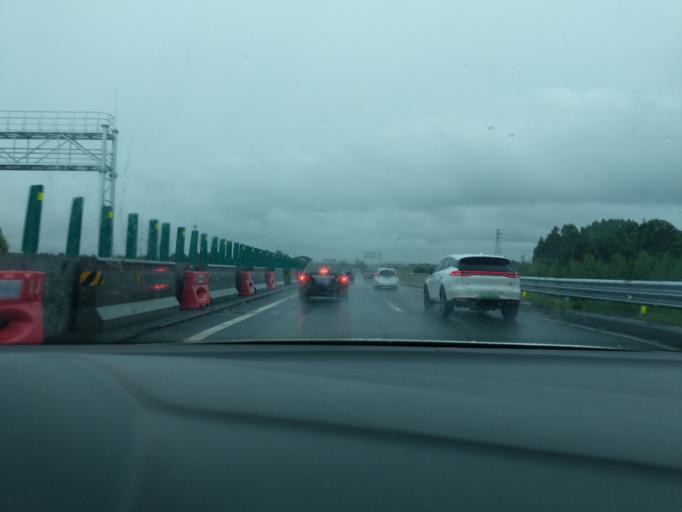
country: CN
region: Guangdong
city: Yueshan
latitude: 22.4632
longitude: 112.6932
